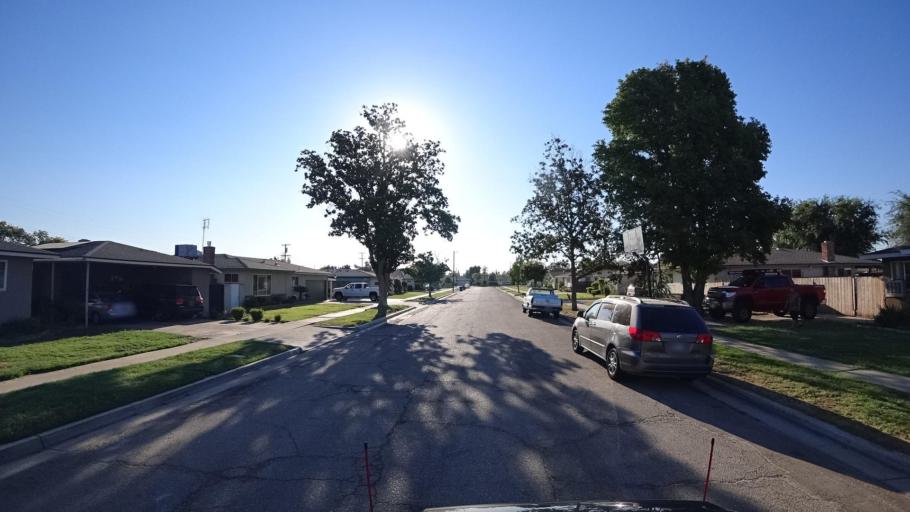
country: US
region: California
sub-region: Fresno County
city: Fresno
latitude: 36.7760
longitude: -119.8336
